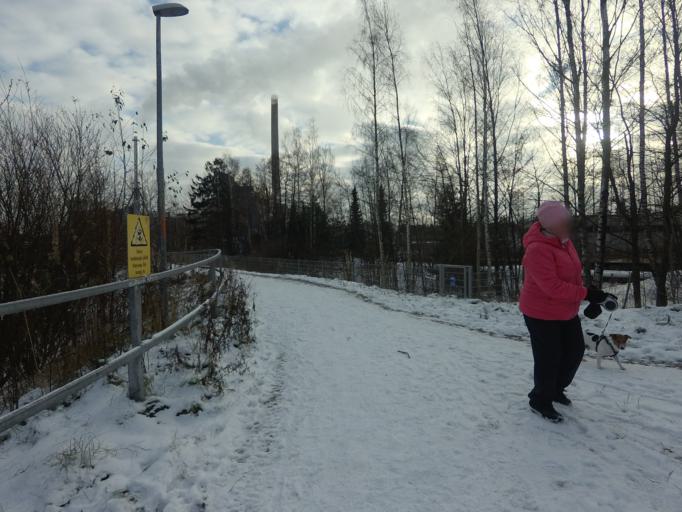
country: FI
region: Uusimaa
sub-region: Helsinki
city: Koukkuniemi
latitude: 60.1515
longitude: 24.7130
